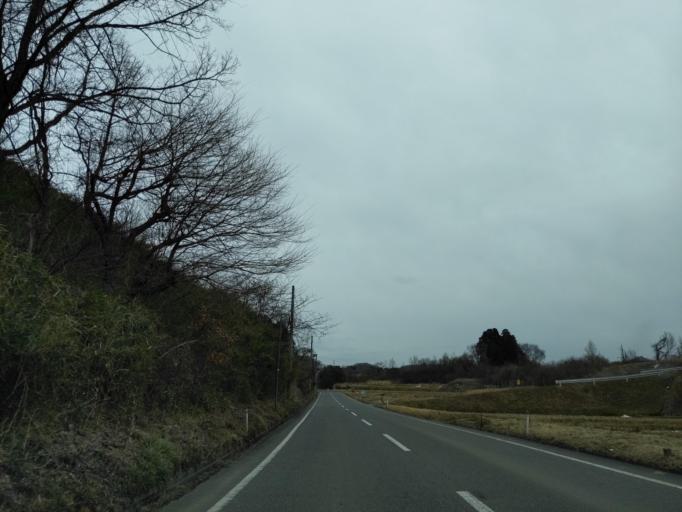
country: JP
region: Fukushima
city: Miharu
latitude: 37.4611
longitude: 140.4348
